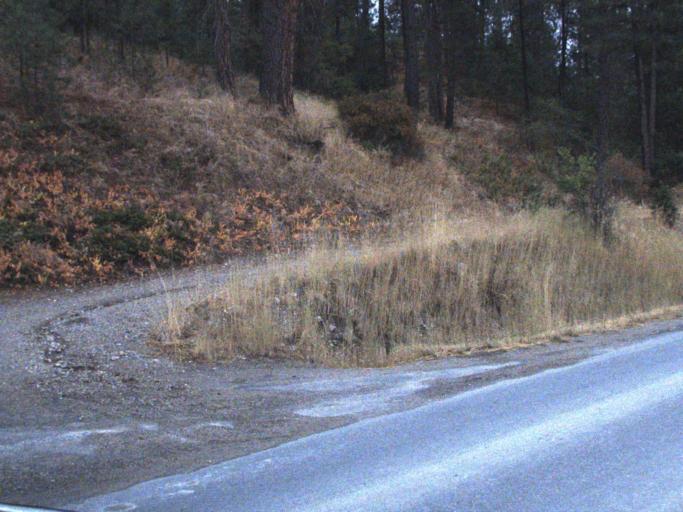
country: US
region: Washington
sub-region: Stevens County
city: Chewelah
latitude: 48.1722
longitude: -117.7232
